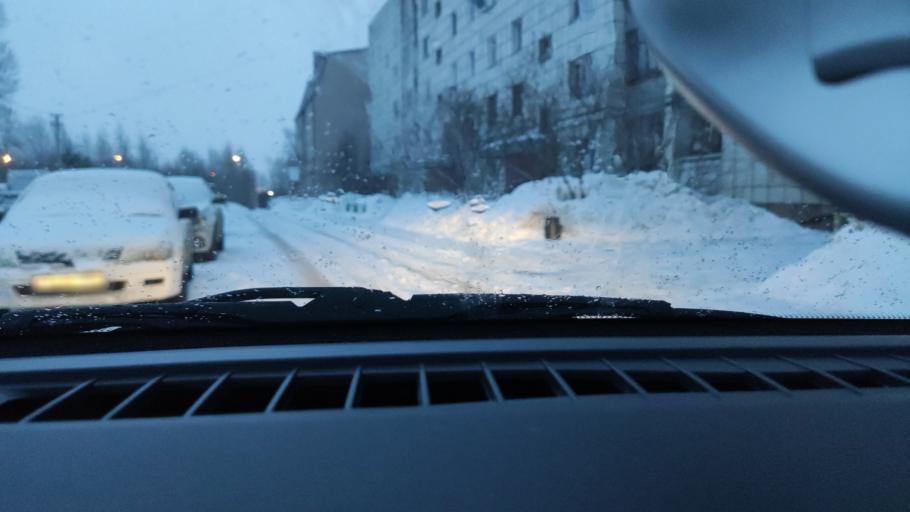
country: RU
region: Perm
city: Kondratovo
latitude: 58.0023
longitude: 56.1201
